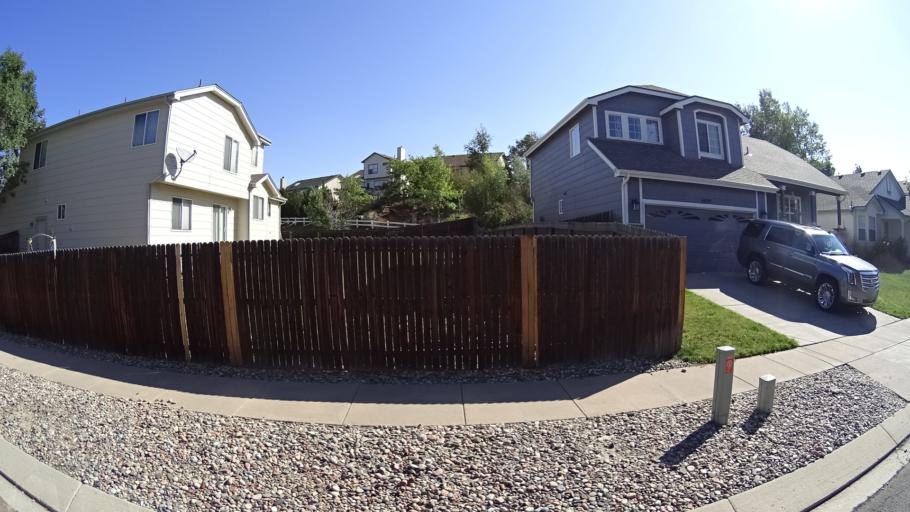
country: US
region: Colorado
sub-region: El Paso County
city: Cimarron Hills
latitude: 38.8825
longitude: -104.7062
